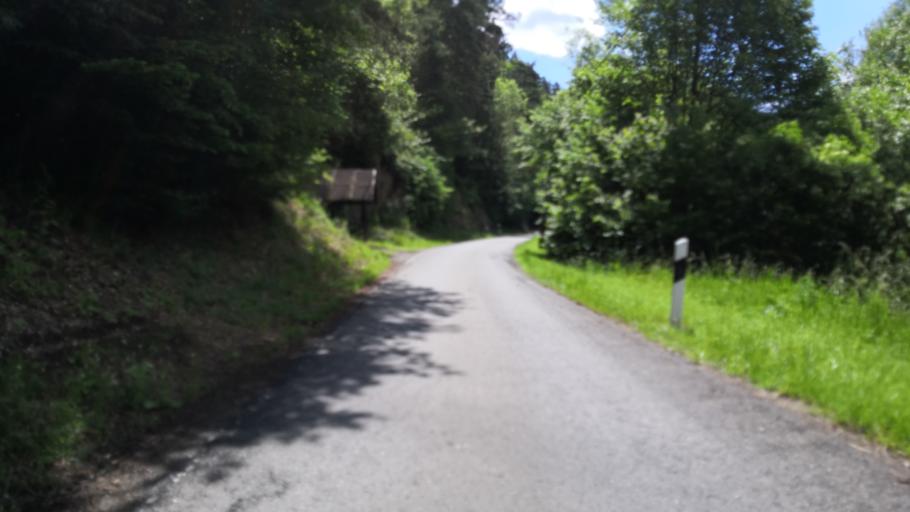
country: DE
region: Thuringia
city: Probstzella
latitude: 50.5710
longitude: 11.3725
